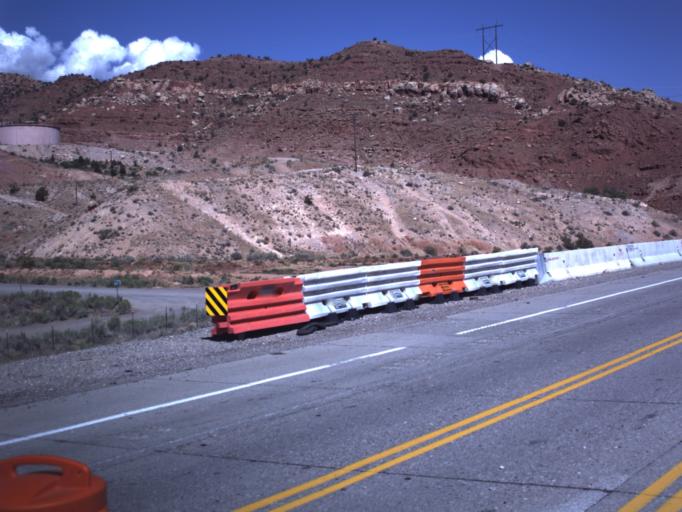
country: US
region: Utah
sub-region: Sevier County
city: Richfield
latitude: 38.7716
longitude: -112.0995
